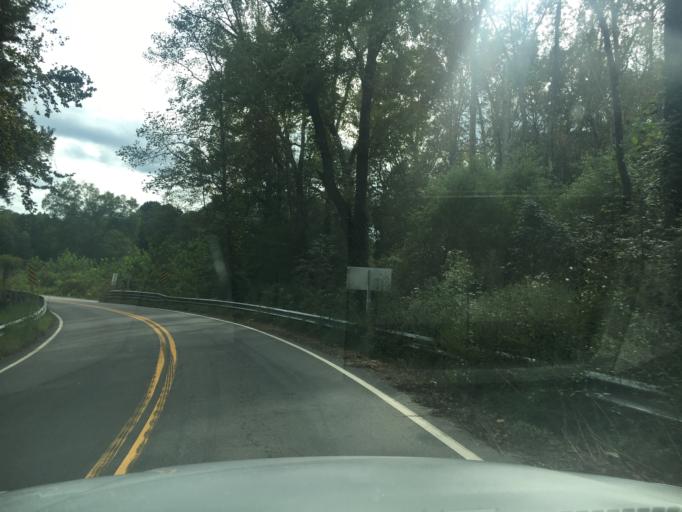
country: US
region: South Carolina
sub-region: Spartanburg County
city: Wellford
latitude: 34.9256
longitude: -82.0627
